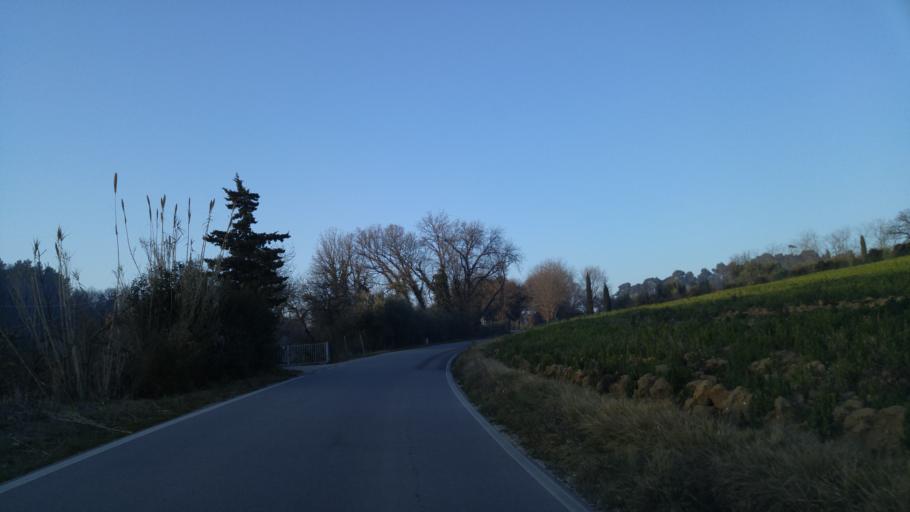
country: IT
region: The Marches
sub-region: Provincia di Pesaro e Urbino
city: Fenile
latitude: 43.8586
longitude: 12.9629
